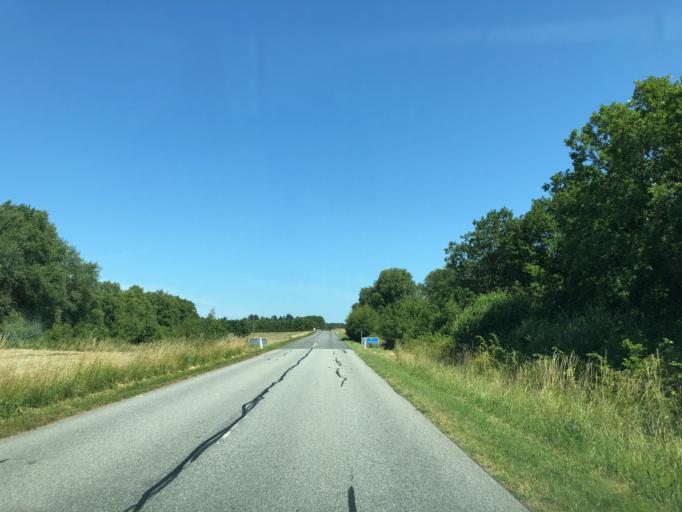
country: DK
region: Central Jutland
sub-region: Skive Kommune
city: Skive
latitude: 56.5225
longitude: 9.0311
